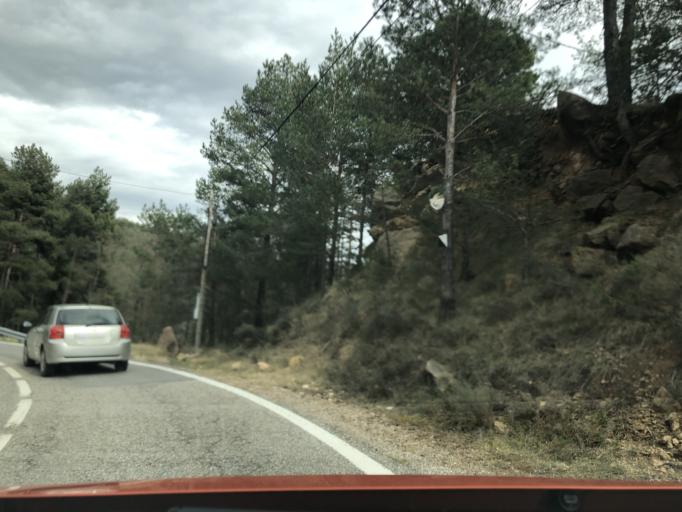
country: ES
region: Catalonia
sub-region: Provincia de Barcelona
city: Castellar del Riu
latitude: 42.0946
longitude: 1.7862
